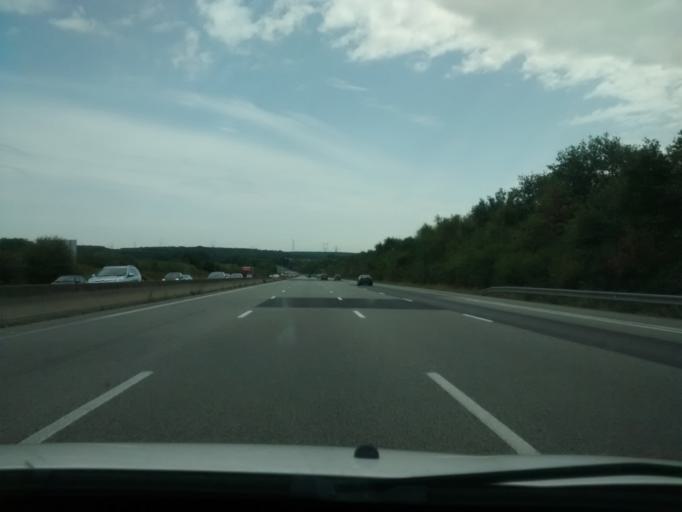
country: FR
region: Ile-de-France
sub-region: Departement de l'Essonne
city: Vaugrigneuse
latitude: 48.6105
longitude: 2.1056
